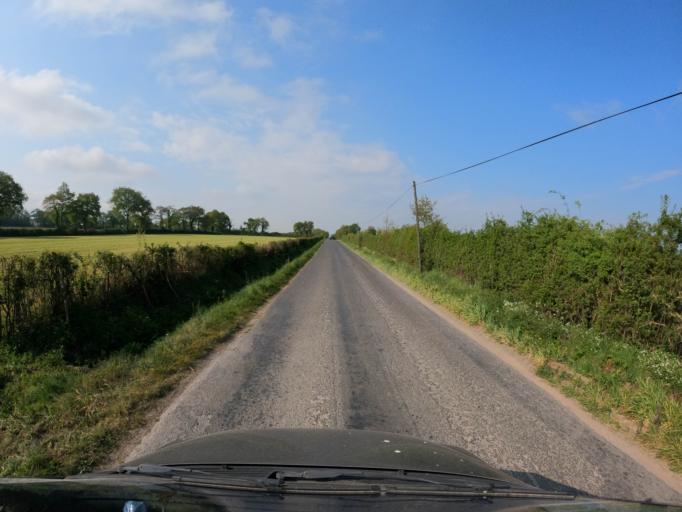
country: FR
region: Pays de la Loire
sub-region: Departement de Maine-et-Loire
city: Torfou
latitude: 47.0506
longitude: -1.0963
